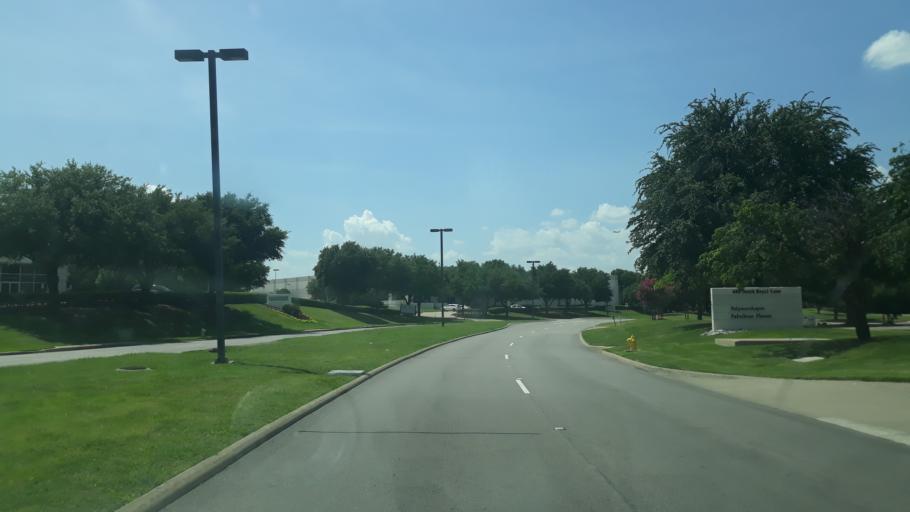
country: US
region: Texas
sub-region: Dallas County
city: Coppell
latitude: 32.9585
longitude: -97.0254
